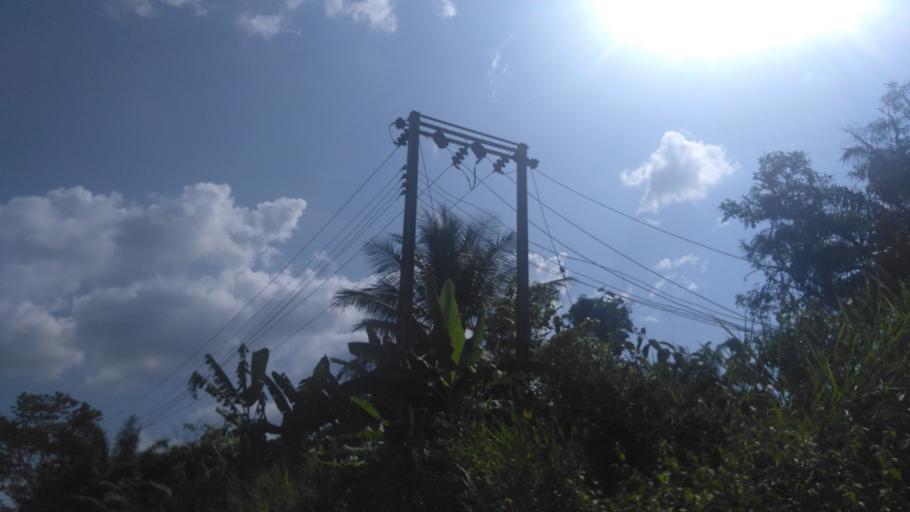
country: NG
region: Osun
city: Ifetedo
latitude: 7.0240
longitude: 4.6302
